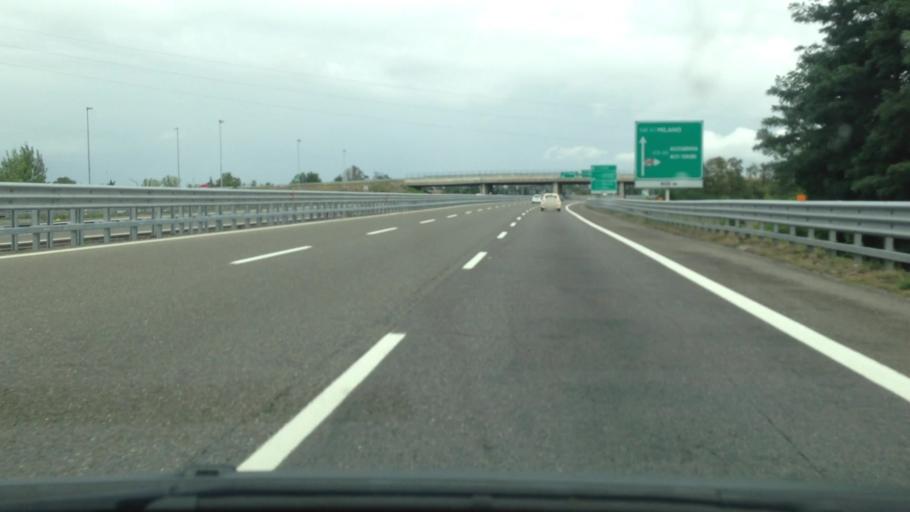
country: IT
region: Piedmont
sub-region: Provincia di Alessandria
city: Tortona
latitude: 44.9177
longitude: 8.8447
